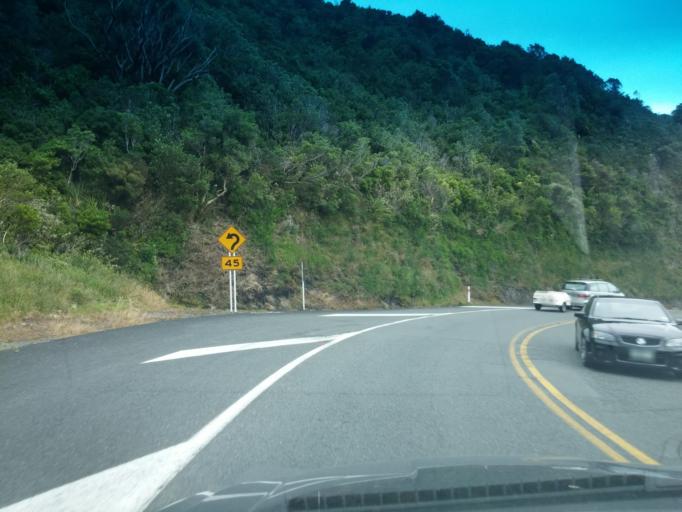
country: NZ
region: Wellington
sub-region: Upper Hutt City
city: Upper Hutt
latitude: -41.1141
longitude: 175.2185
